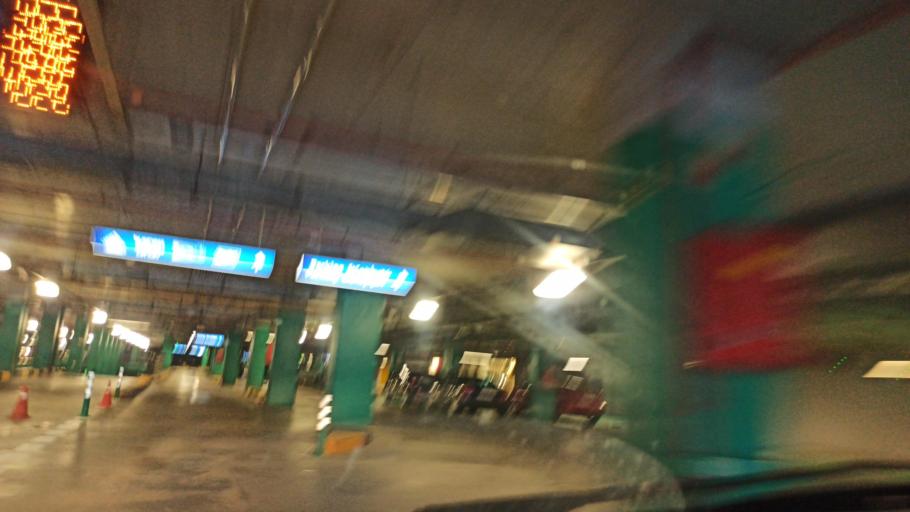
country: ES
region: Galicia
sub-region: Provincia da Coruna
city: A Coruna
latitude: 43.3449
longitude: -8.4268
